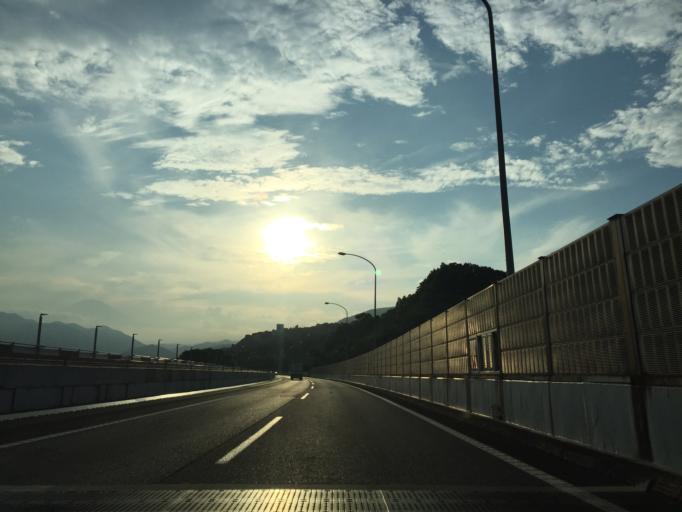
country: JP
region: Kanagawa
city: Hadano
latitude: 35.3478
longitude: 139.1504
